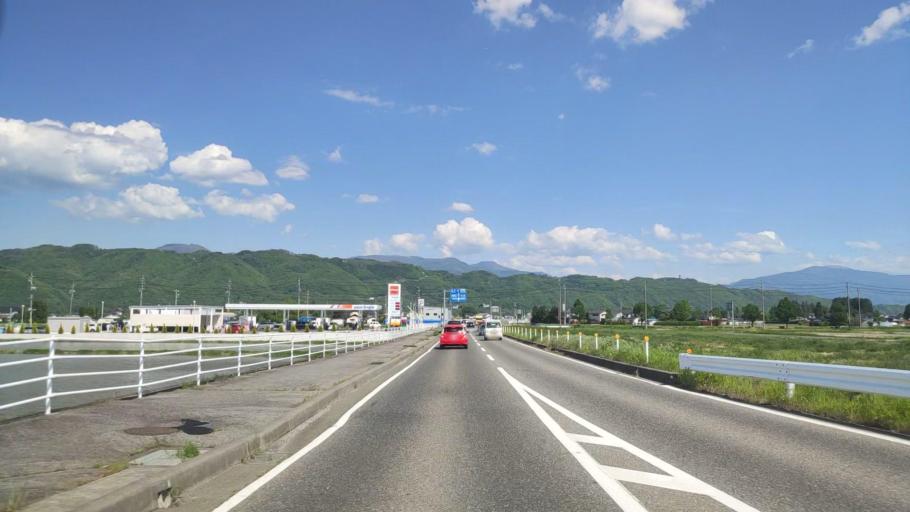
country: JP
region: Nagano
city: Toyoshina
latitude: 36.2803
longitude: 137.9186
